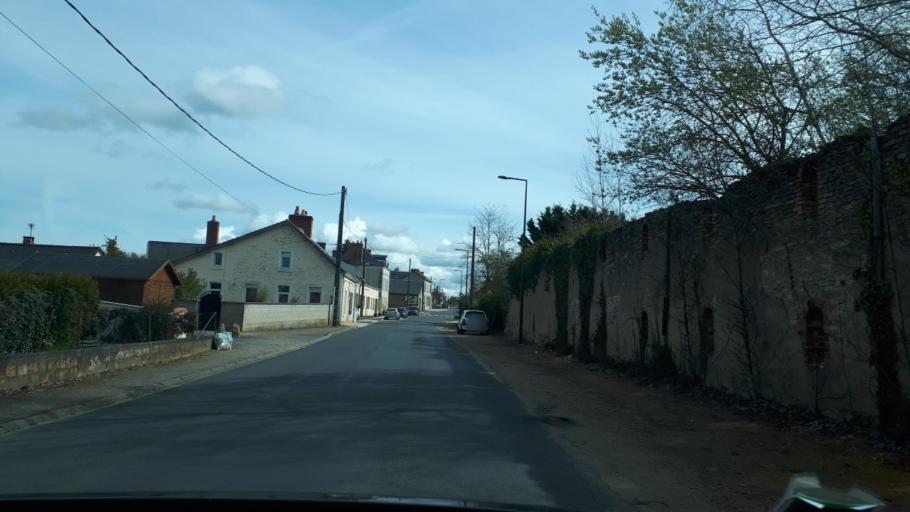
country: FR
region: Pays de la Loire
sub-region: Departement de la Sarthe
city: Ecommoy
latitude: 47.8250
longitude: 0.2647
